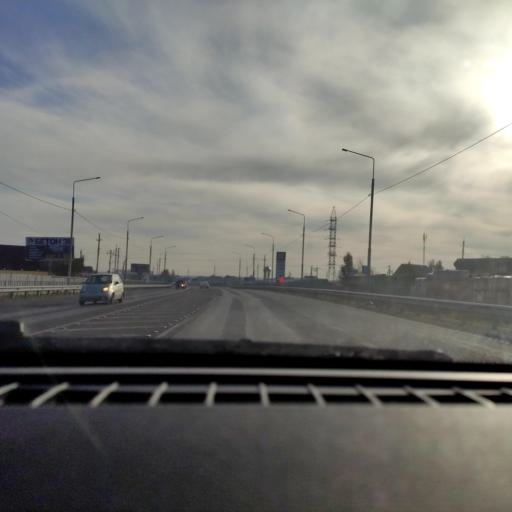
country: RU
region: Voronezj
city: Somovo
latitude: 51.6772
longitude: 39.3292
